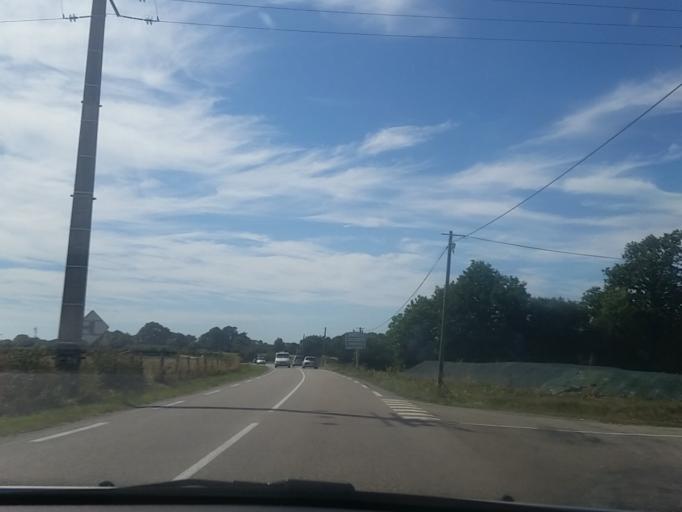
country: FR
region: Pays de la Loire
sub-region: Departement de la Loire-Atlantique
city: Chauve
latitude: 47.1909
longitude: -1.9962
